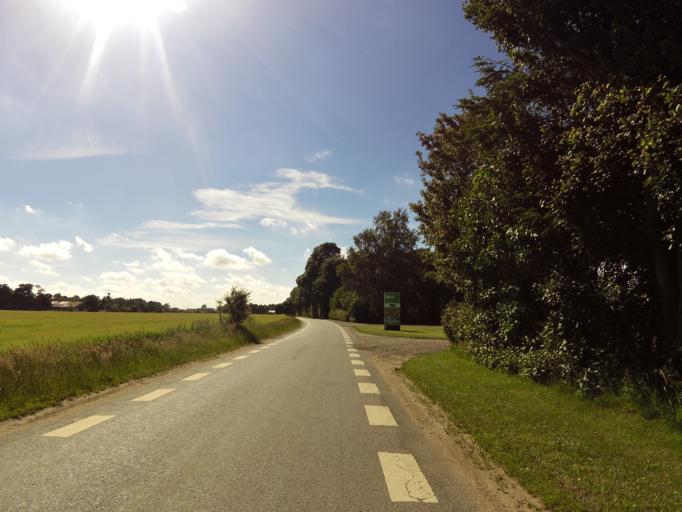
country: DK
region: South Denmark
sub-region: Aabenraa Kommune
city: Rodekro
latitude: 55.0669
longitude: 9.2371
